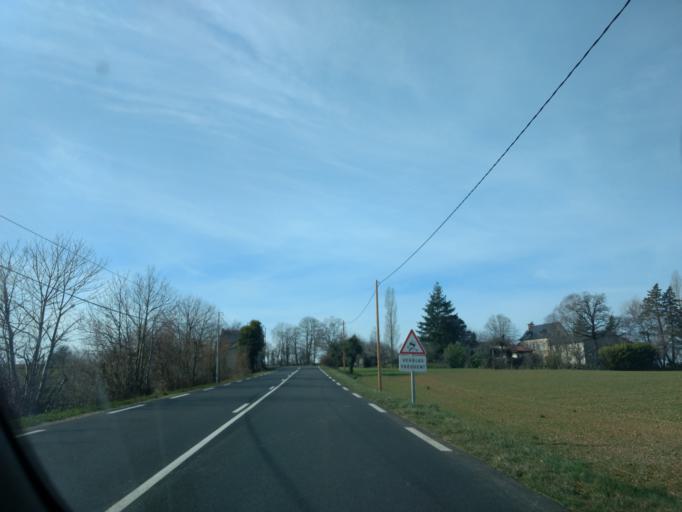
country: FR
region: Midi-Pyrenees
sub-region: Departement de l'Aveyron
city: Villeneuve
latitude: 44.4195
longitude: 2.1064
